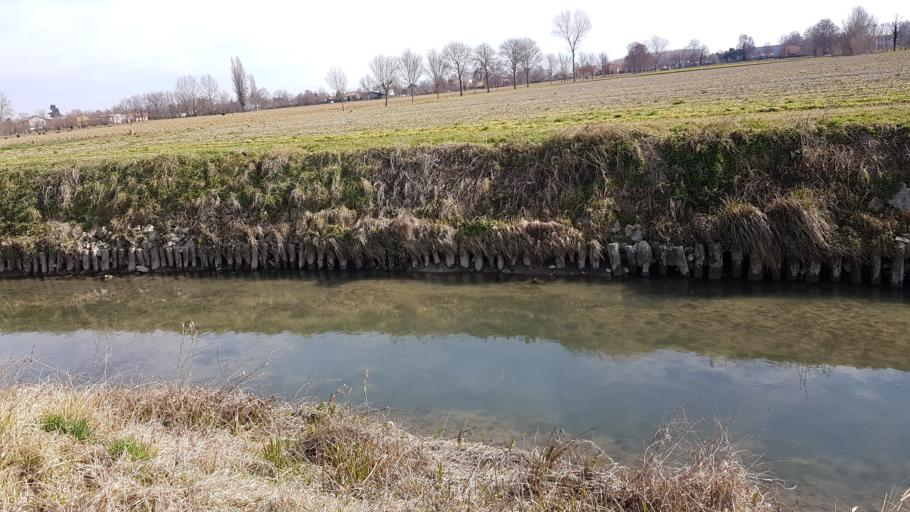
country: IT
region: Veneto
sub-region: Provincia di Padova
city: San Giorgio delle Pertiche
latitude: 45.5498
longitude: 11.9049
